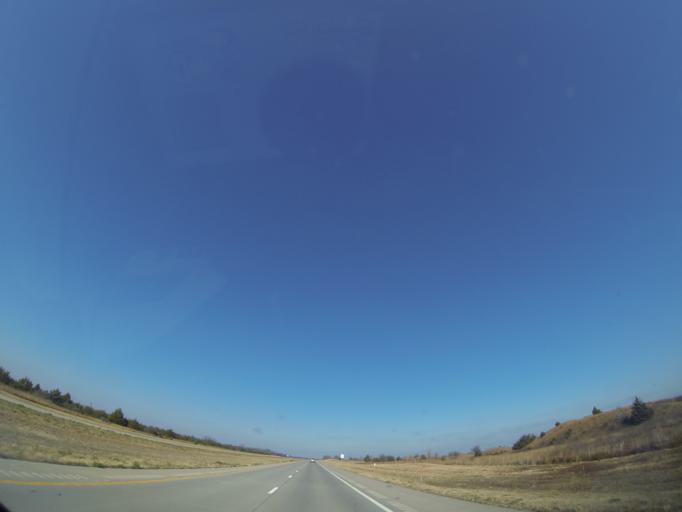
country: US
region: Kansas
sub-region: Reno County
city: Hutchinson
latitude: 38.1230
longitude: -97.8754
